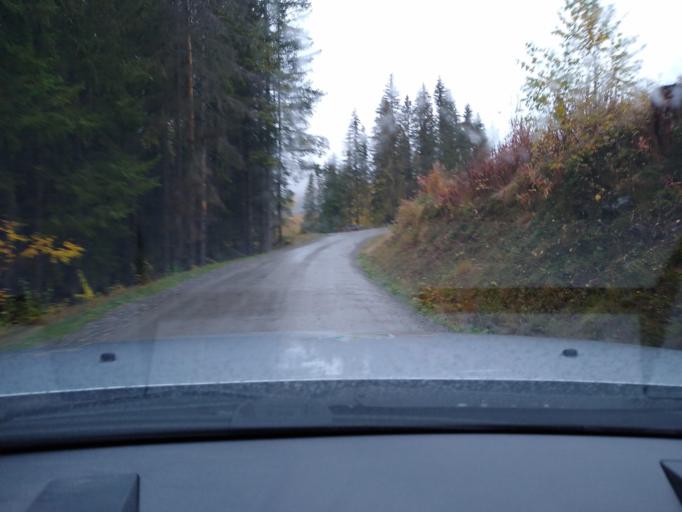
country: NO
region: Oppland
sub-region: Ringebu
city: Ringebu
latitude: 61.5409
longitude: 10.1493
